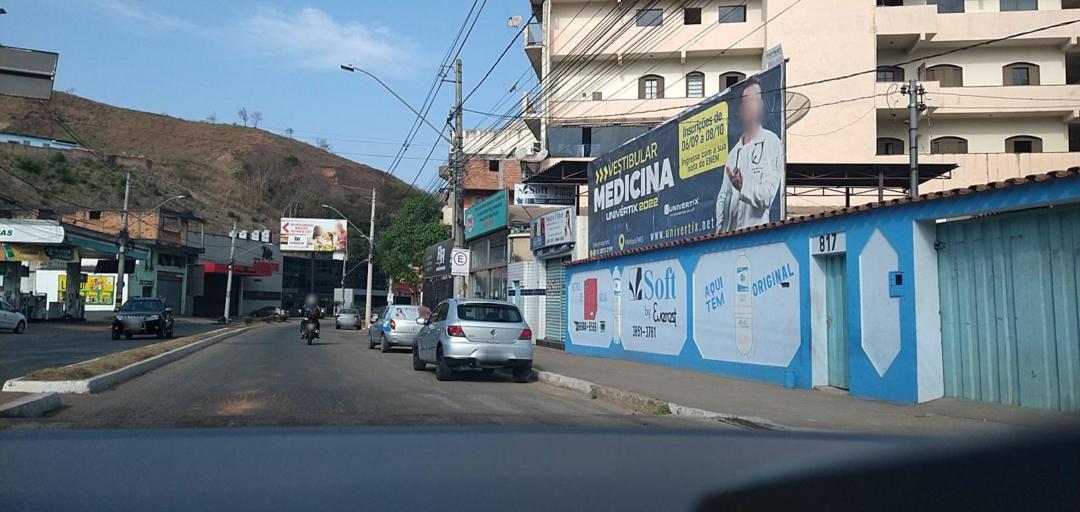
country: BR
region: Minas Gerais
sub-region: Joao Monlevade
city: Joao Monlevade
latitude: -19.8090
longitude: -43.1708
